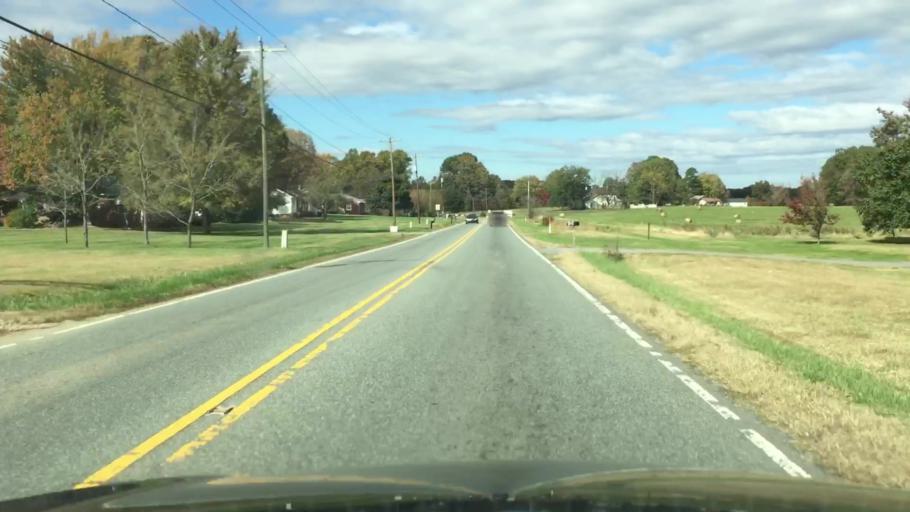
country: US
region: North Carolina
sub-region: Iredell County
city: Mooresville
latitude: 35.6297
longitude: -80.8242
